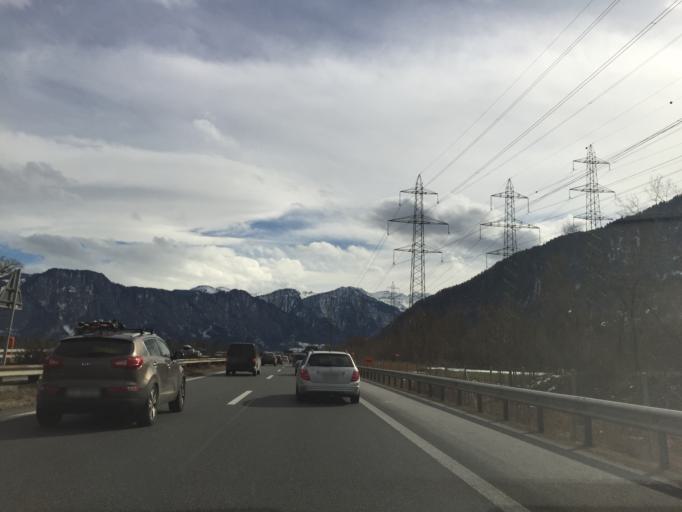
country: CH
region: Grisons
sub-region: Landquart District
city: Maienfeld
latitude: 46.9976
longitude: 9.5250
